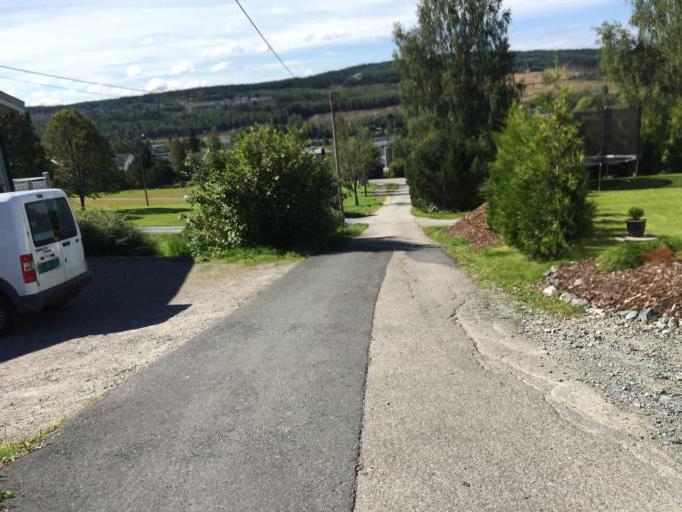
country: NO
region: Hedmark
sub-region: Kongsvinger
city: Kongsvinger
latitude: 60.2053
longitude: 11.9774
